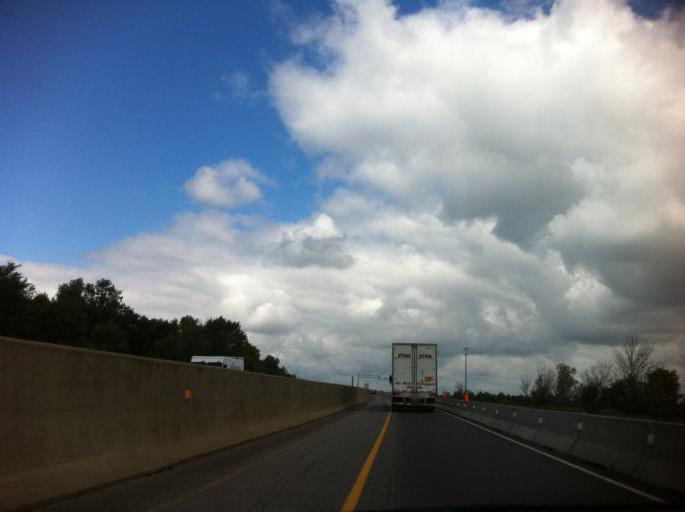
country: US
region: Ohio
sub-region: Trumbull County
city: Lordstown
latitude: 41.1255
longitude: -80.8511
